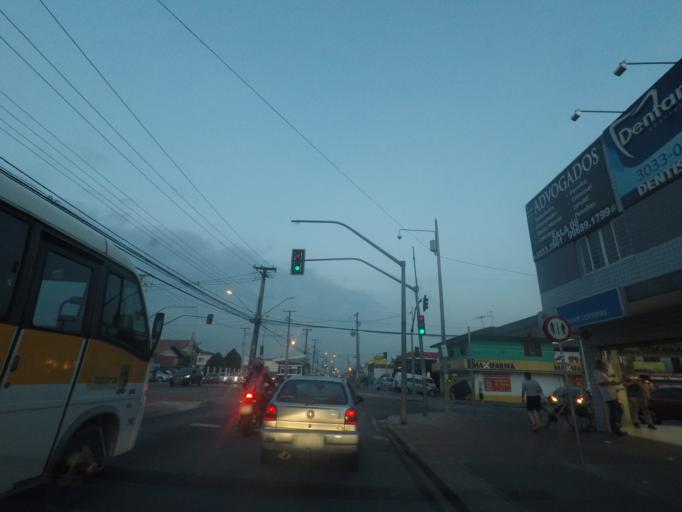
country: BR
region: Parana
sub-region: Pinhais
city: Pinhais
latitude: -25.4494
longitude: -49.1832
